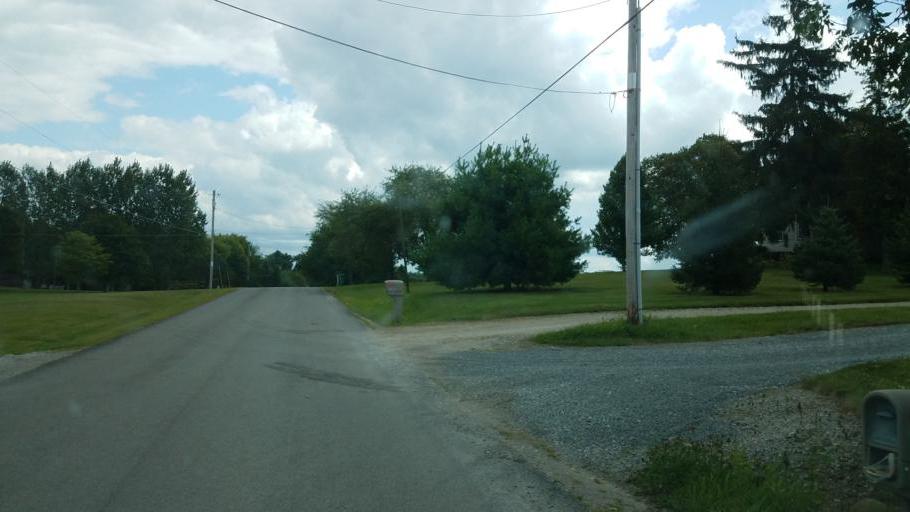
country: US
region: Ohio
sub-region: Morrow County
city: Cardington
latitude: 40.3932
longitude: -82.8049
